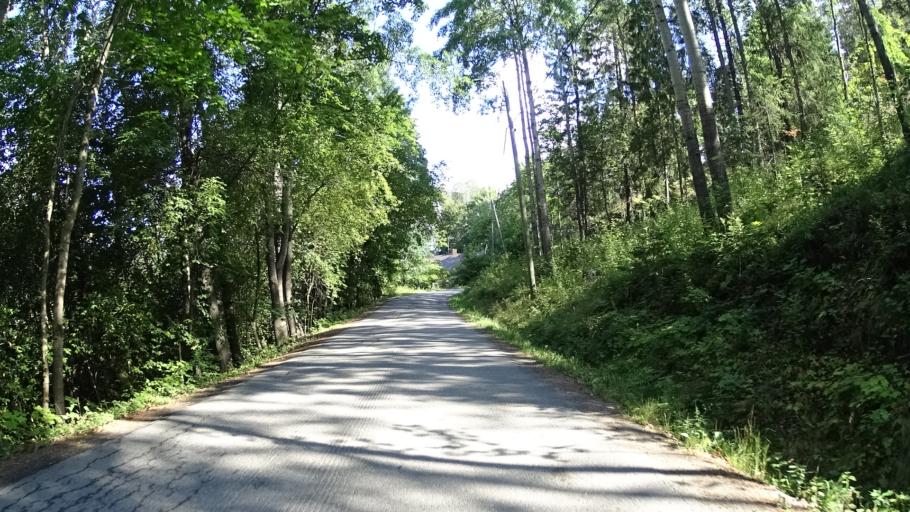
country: FI
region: Uusimaa
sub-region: Helsinki
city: Espoo
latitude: 60.1821
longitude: 24.5914
